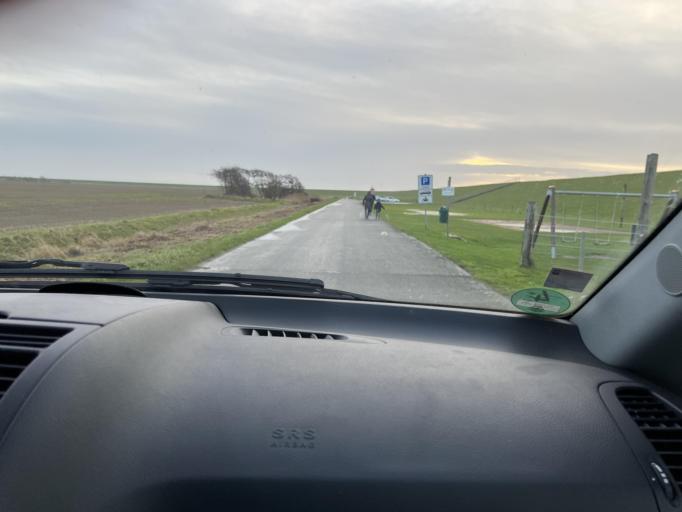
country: DE
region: Schleswig-Holstein
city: Hedwigenkoog
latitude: 54.1803
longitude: 8.8123
